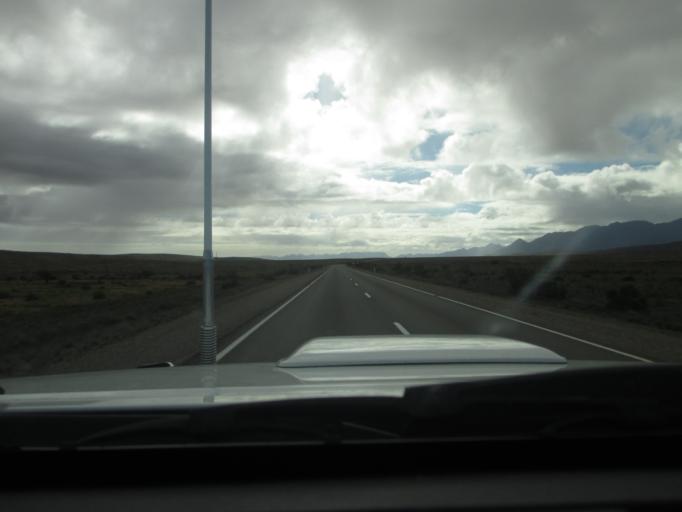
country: AU
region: South Australia
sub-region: Flinders Ranges
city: Quorn
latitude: -31.6059
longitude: 138.4002
